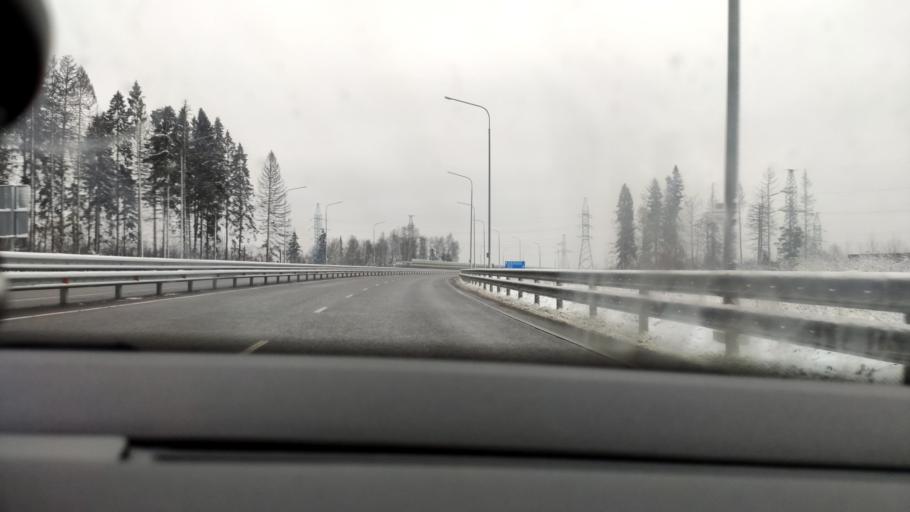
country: RU
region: Moskovskaya
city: Solnechnogorsk
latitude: 56.1637
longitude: 36.9183
